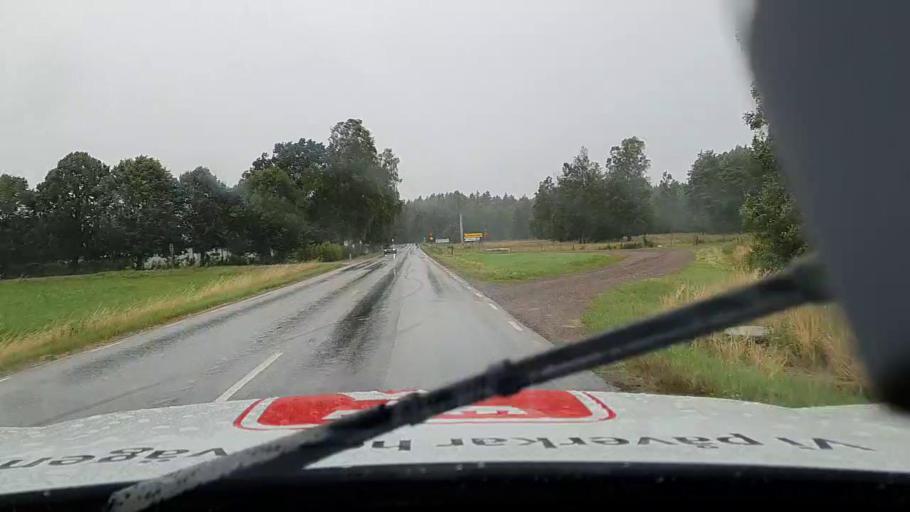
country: SE
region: Vaestra Goetaland
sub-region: Toreboda Kommun
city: Toereboda
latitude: 58.6798
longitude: 14.1323
